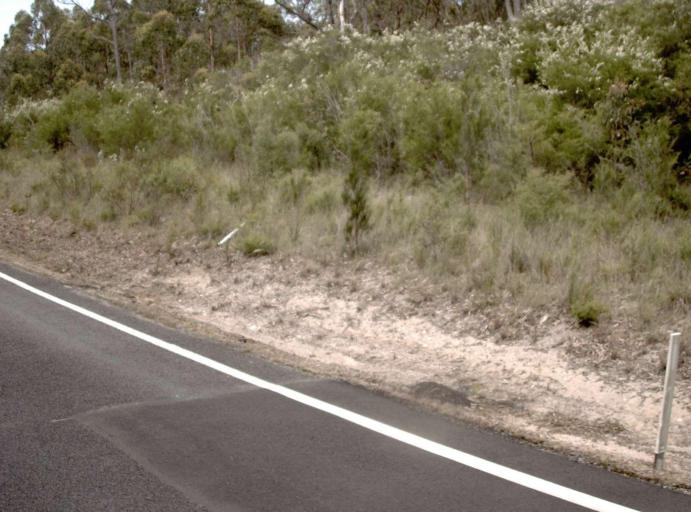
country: AU
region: New South Wales
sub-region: Bega Valley
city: Eden
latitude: -37.4857
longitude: 149.5504
